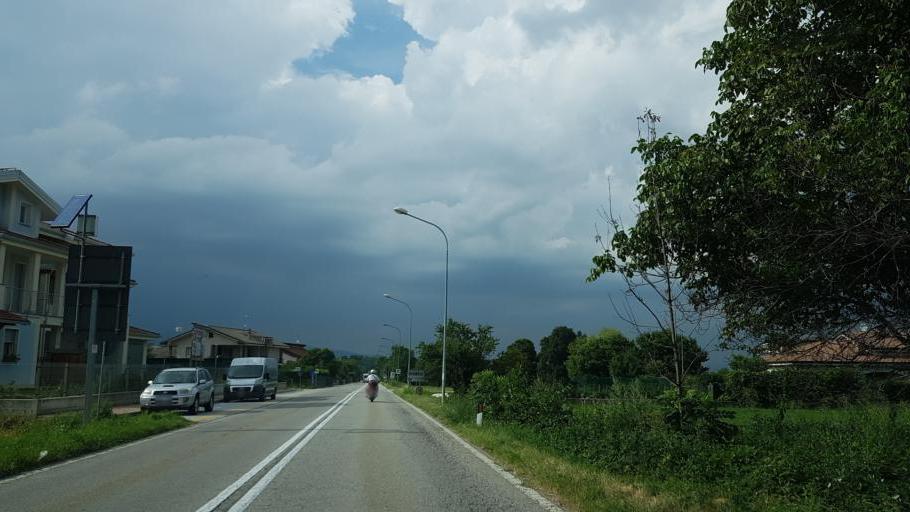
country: IT
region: Piedmont
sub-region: Provincia di Cuneo
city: Vignolo
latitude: 44.3566
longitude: 7.4783
